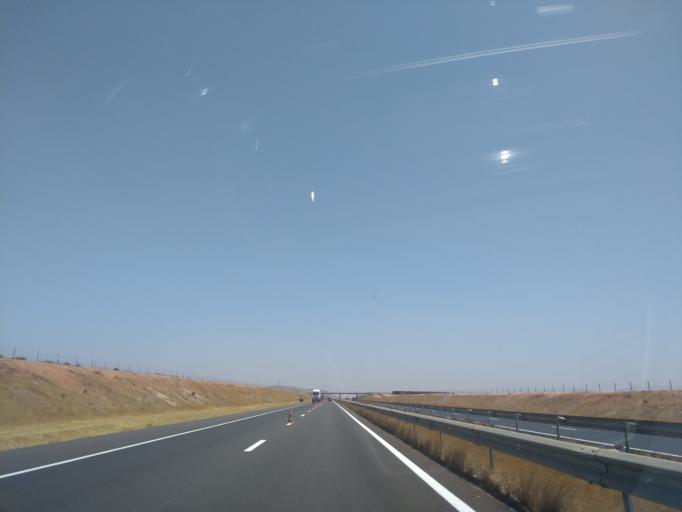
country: MA
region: Marrakech-Tensift-Al Haouz
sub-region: Kelaa-Des-Sraghna
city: Sidi Abdallah
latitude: 32.4325
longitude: -7.9313
